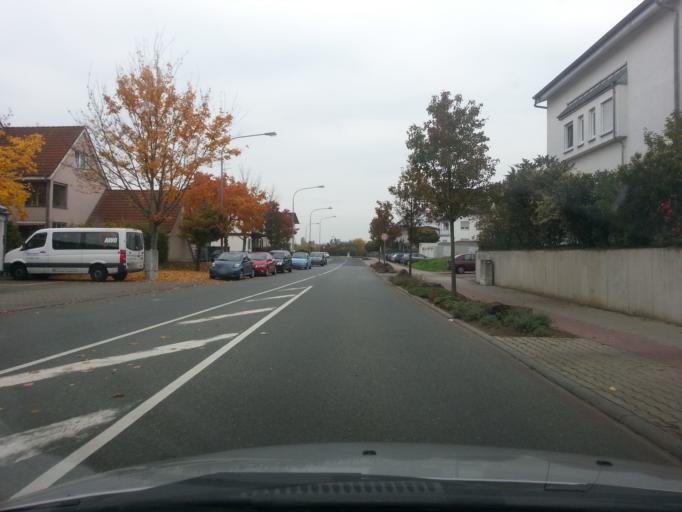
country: DE
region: Hesse
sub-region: Regierungsbezirk Darmstadt
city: Muehlheim am Main
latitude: 50.1248
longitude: 8.8384
